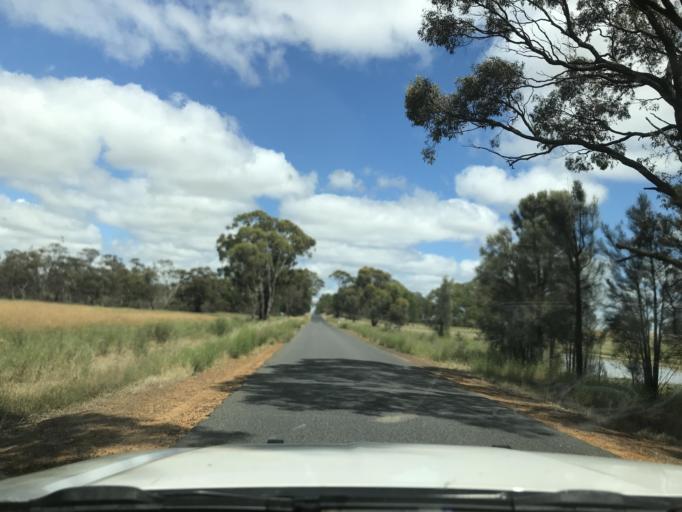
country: AU
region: South Australia
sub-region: Naracoorte and Lucindale
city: Naracoorte
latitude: -36.6828
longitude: 141.3075
